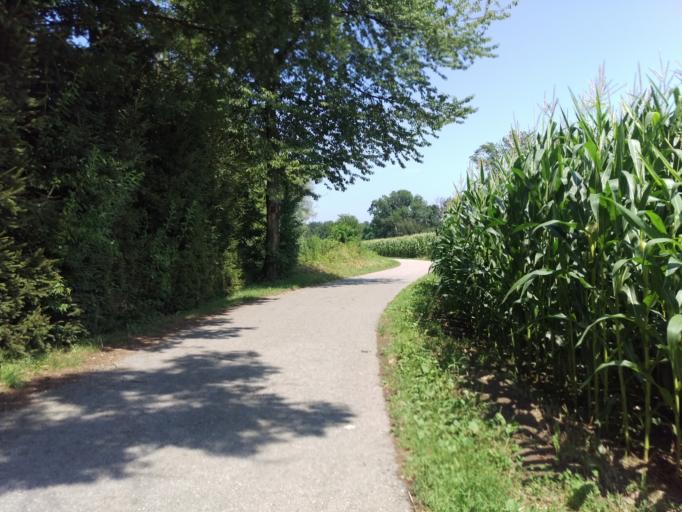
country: AT
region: Styria
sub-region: Politischer Bezirk Graz-Umgebung
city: Gossendorf
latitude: 46.9925
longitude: 15.4632
